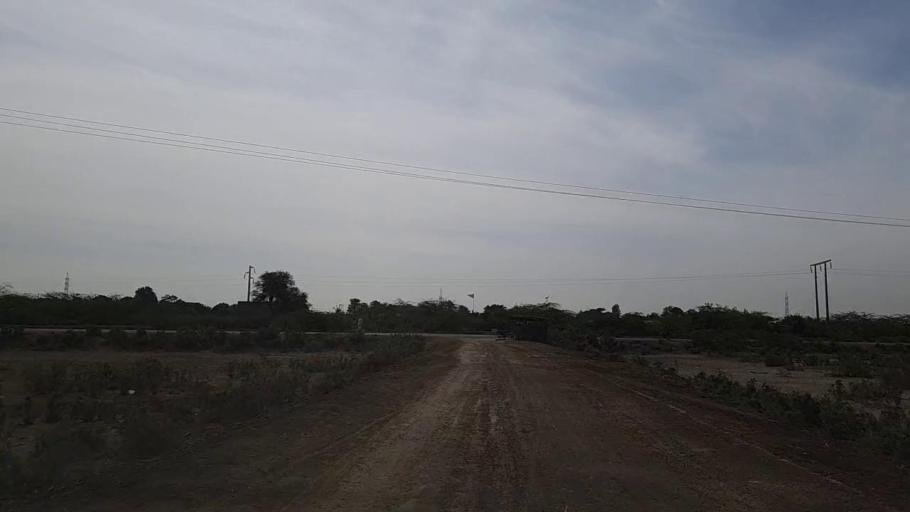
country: PK
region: Sindh
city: Samaro
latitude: 25.2934
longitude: 69.4189
